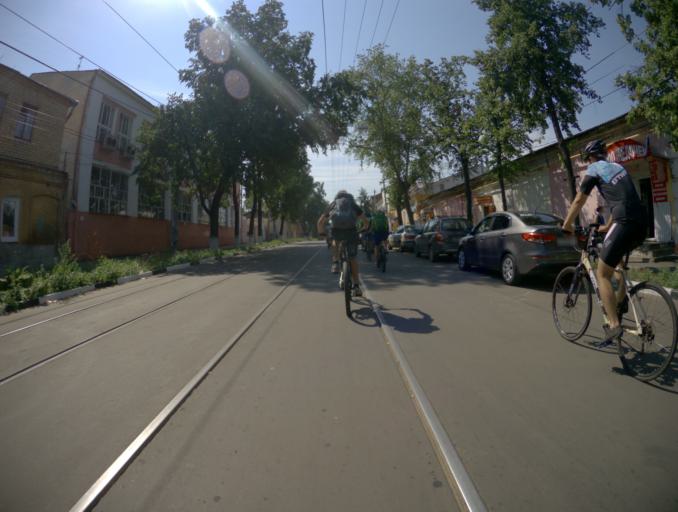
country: RU
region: Nizjnij Novgorod
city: Nizhniy Novgorod
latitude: 56.3206
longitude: 43.9502
